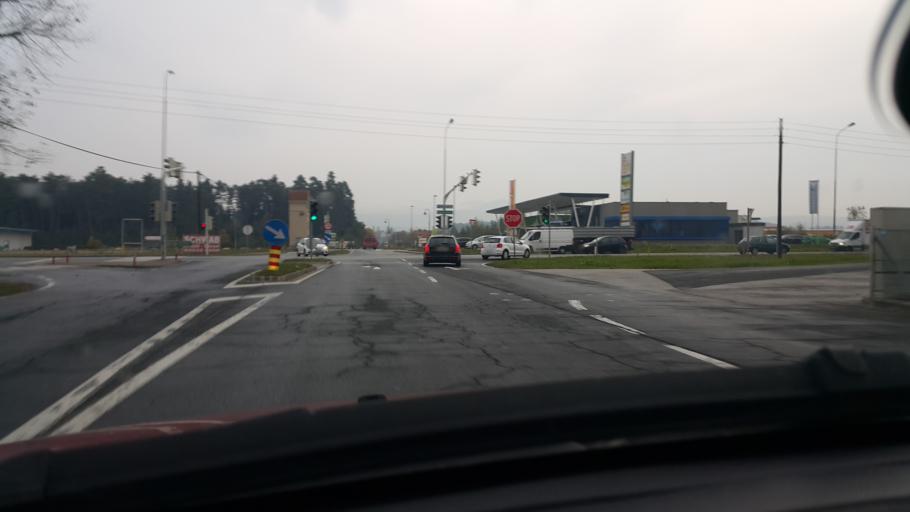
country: AT
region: Carinthia
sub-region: Politischer Bezirk Klagenfurt Land
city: Poggersdorf
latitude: 46.6406
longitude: 14.4508
